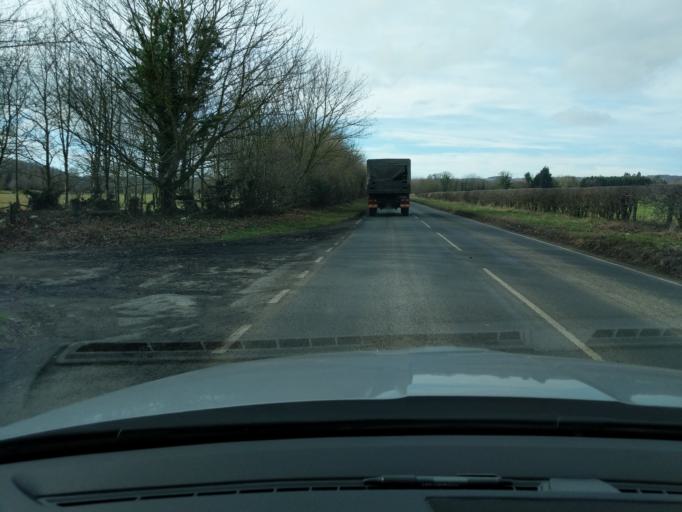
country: GB
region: England
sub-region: North Yorkshire
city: Catterick Garrison
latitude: 54.3951
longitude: -1.6833
